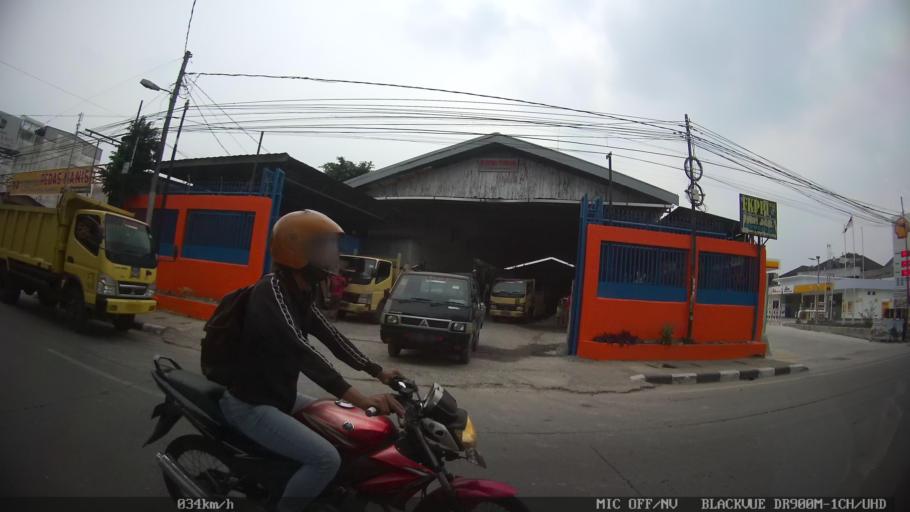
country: ID
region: North Sumatra
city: Medan
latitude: 3.5673
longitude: 98.6918
